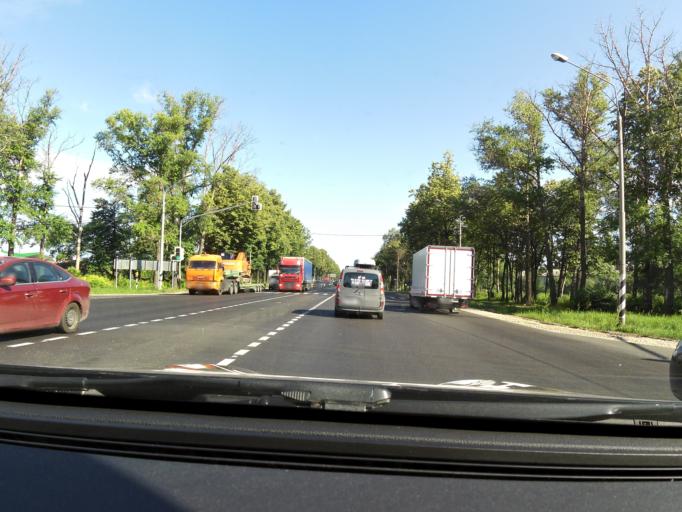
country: RU
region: Tverskaya
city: Zavidovo
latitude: 56.5784
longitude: 36.4960
